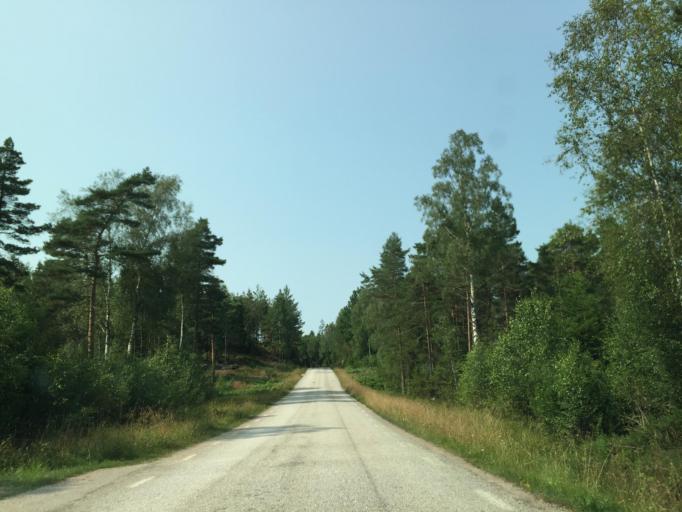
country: SE
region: Vaestra Goetaland
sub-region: Trollhattan
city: Sjuntorp
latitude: 58.3017
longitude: 12.1360
